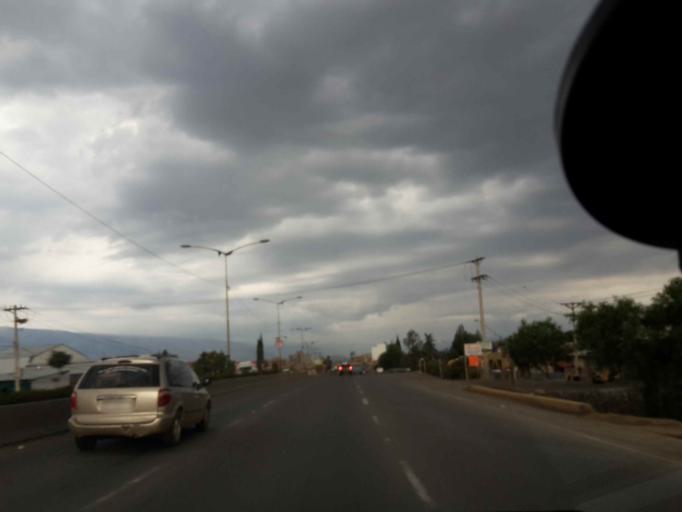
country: BO
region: Cochabamba
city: Sipe Sipe
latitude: -17.3949
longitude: -66.2960
